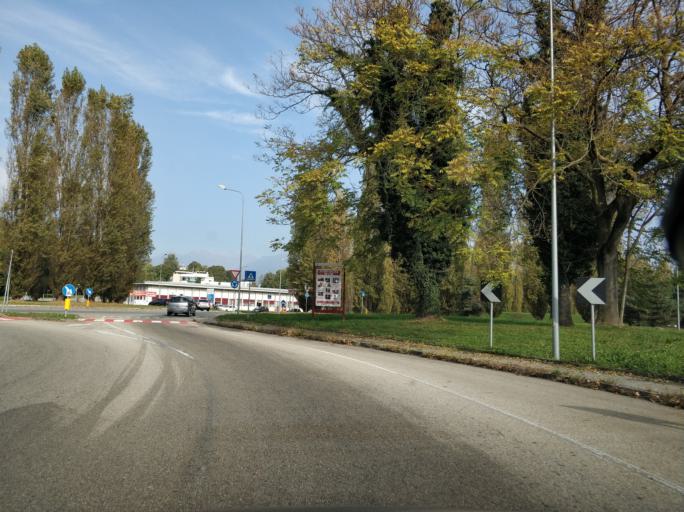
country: IT
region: Piedmont
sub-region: Provincia di Torino
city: Banchette
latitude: 45.4527
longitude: 7.8623
